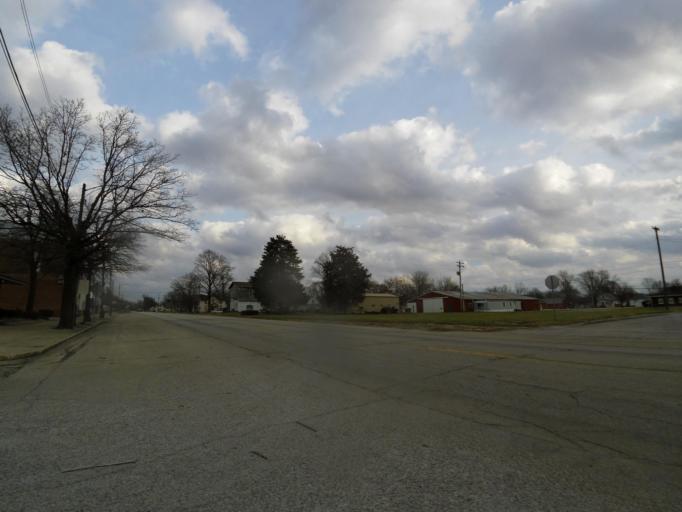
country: US
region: Illinois
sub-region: Fayette County
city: Ramsey
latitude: 39.1423
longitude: -89.1083
